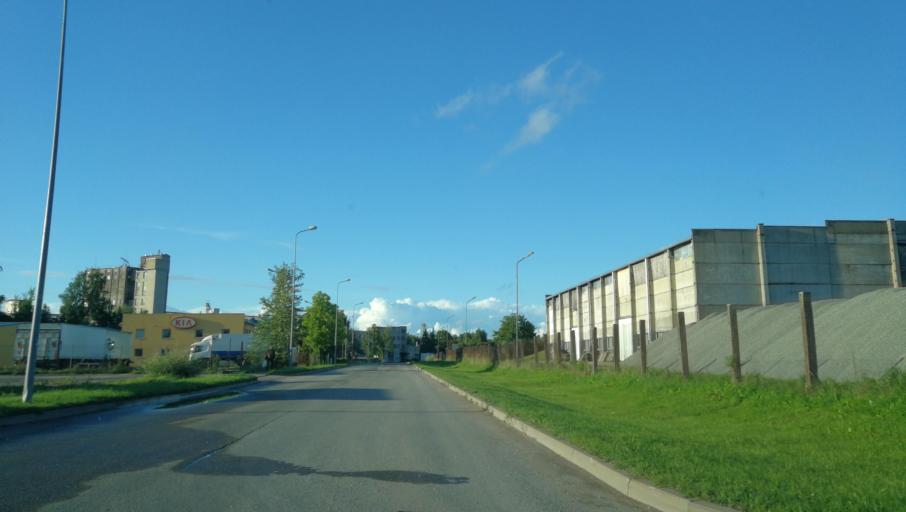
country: LV
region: Valmieras Rajons
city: Valmiera
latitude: 57.5154
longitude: 25.4402
